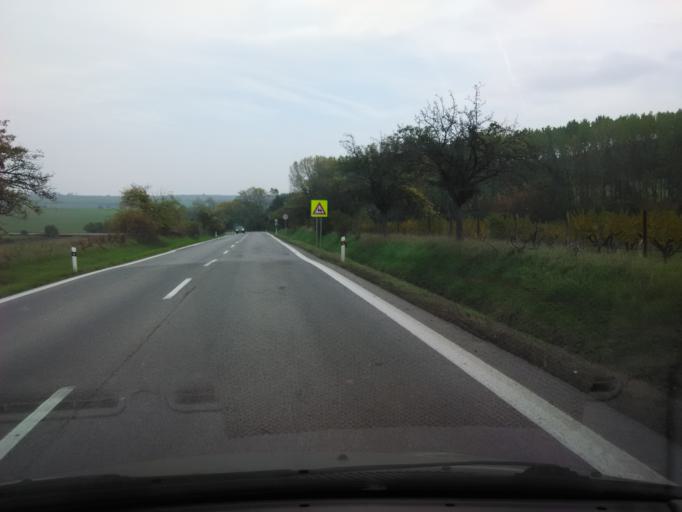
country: SK
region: Nitriansky
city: Svodin
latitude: 48.0328
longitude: 18.4480
